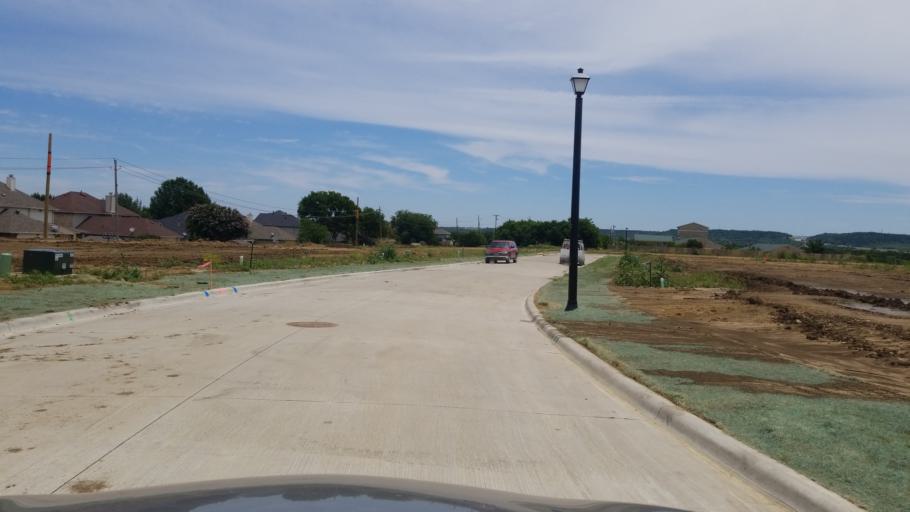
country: US
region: Texas
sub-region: Dallas County
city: Grand Prairie
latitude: 32.6784
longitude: -96.9882
